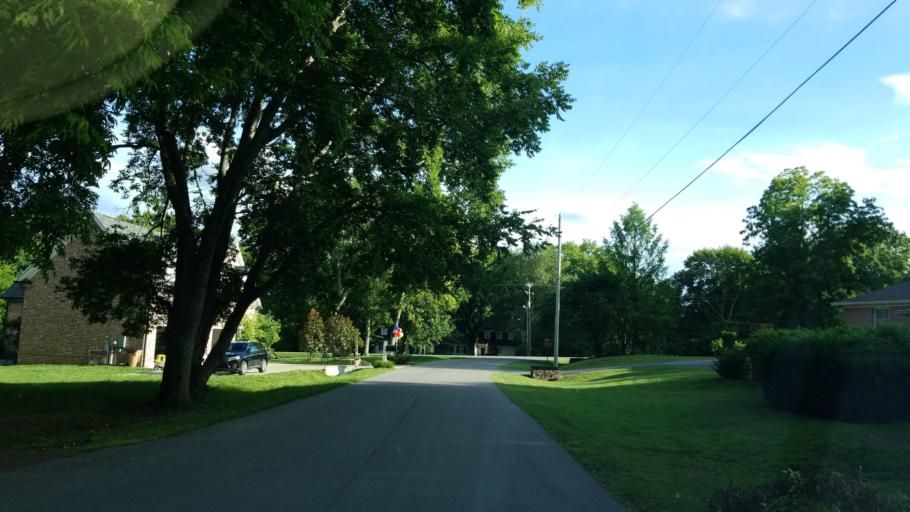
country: US
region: Tennessee
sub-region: Williamson County
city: Brentwood
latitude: 36.0270
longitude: -86.8045
